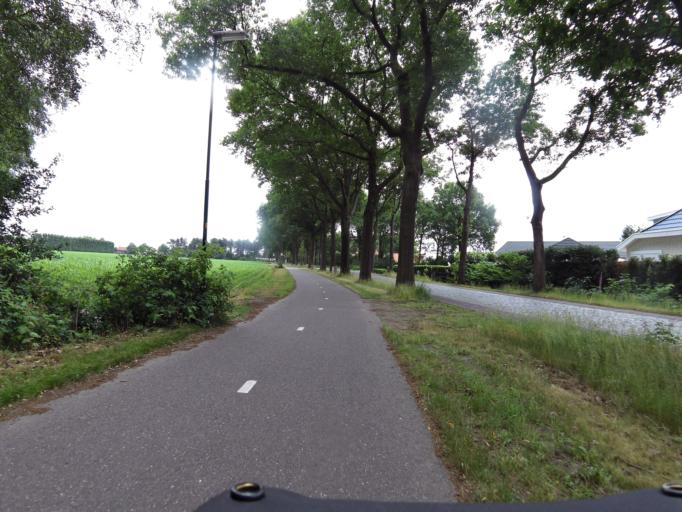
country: NL
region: North Brabant
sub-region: Gemeente Bladel en Netersel
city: Bladel
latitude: 51.3906
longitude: 5.2099
